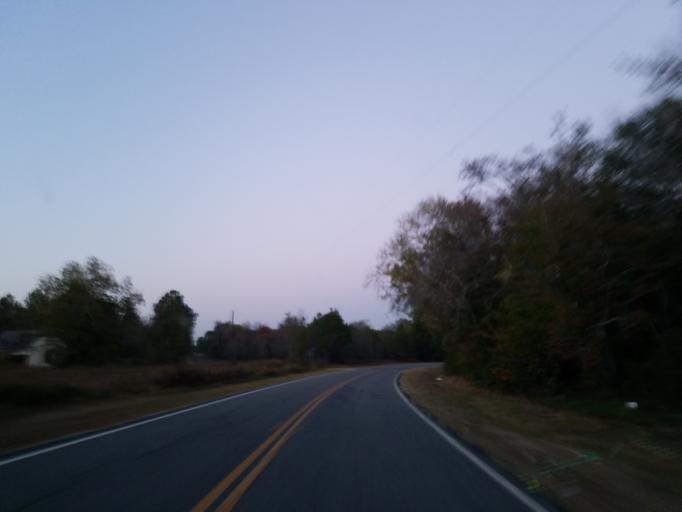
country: US
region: Georgia
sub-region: Wilcox County
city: Rochelle
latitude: 31.8484
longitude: -83.5629
